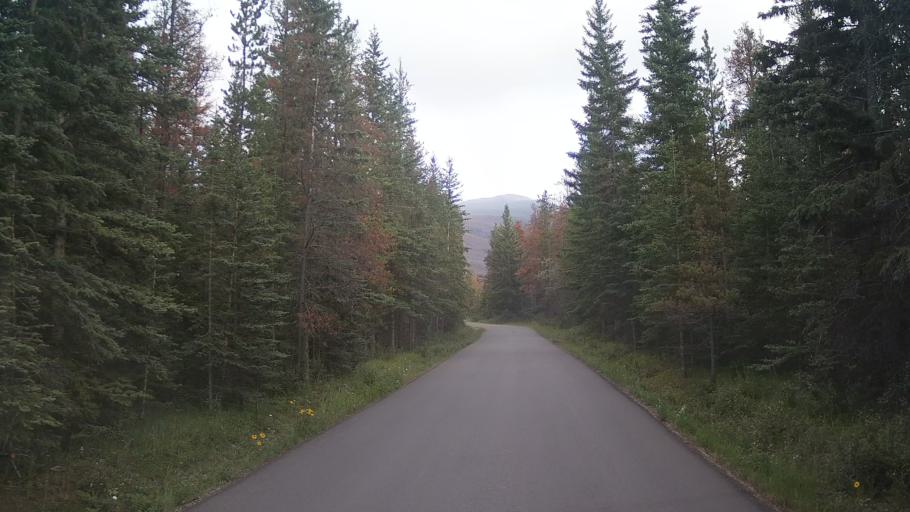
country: CA
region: Alberta
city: Jasper Park Lodge
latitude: 52.9309
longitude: -118.0319
